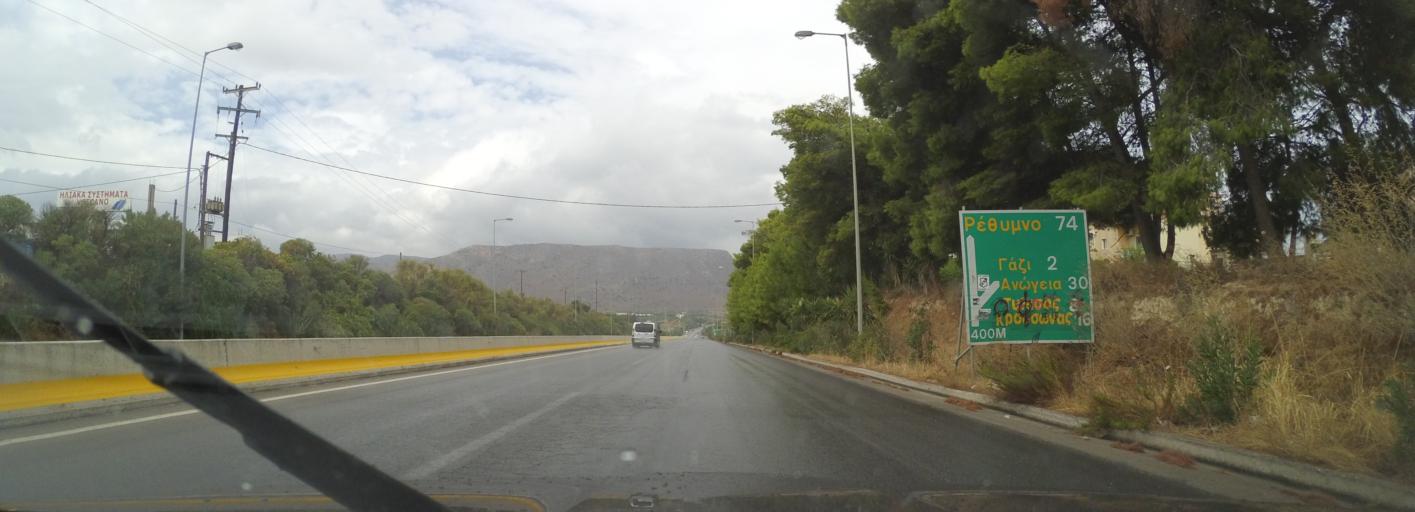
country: GR
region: Crete
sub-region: Nomos Irakleiou
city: Gazi
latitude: 35.3194
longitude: 25.0682
